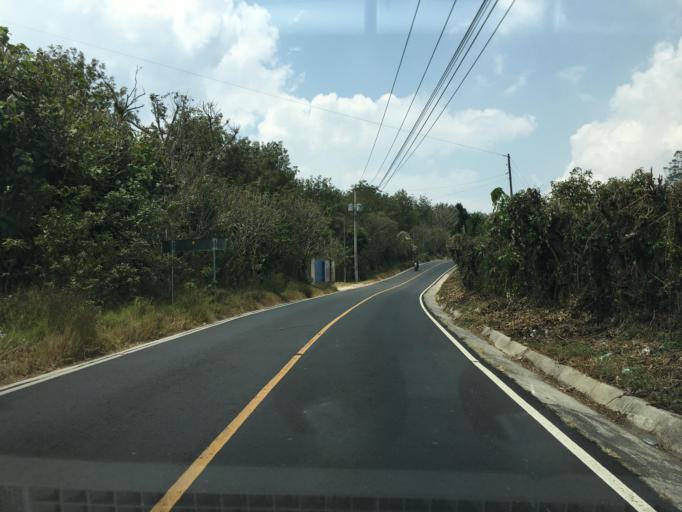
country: GT
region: Guatemala
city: Villa Canales
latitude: 14.4093
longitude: -90.5365
